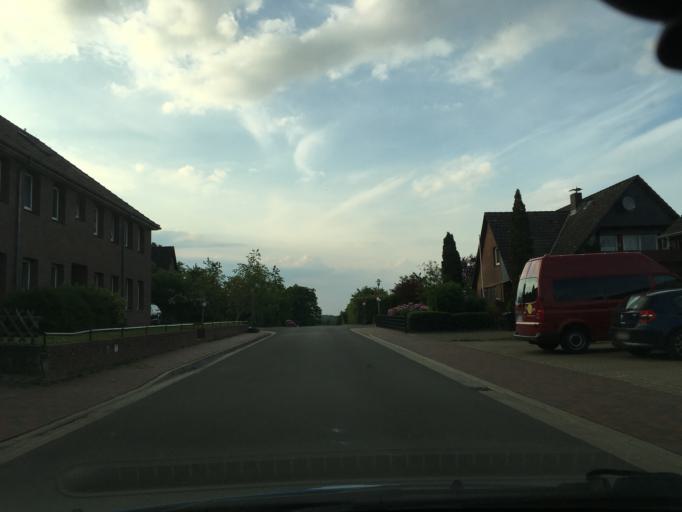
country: DE
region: Lower Saxony
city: Amelinghausen
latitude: 53.1297
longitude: 10.2107
